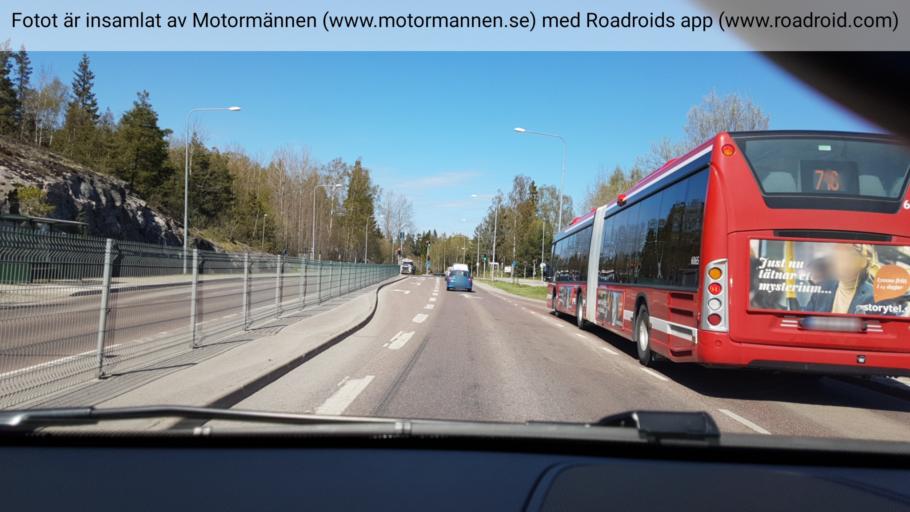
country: SE
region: Stockholm
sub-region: Botkyrka Kommun
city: Varsta
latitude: 59.1819
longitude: 17.8150
